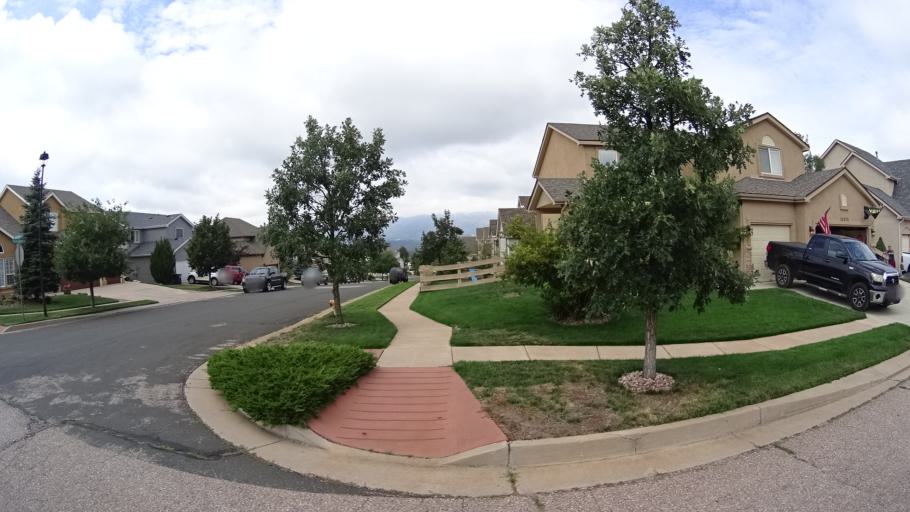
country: US
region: Colorado
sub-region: El Paso County
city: Gleneagle
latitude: 39.0150
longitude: -104.8061
